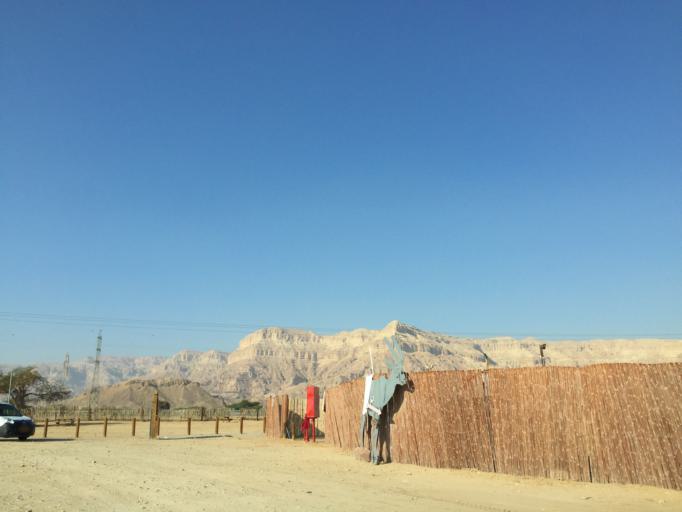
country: JO
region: Ma'an
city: Al Quwayrah
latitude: 29.8459
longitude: 35.0289
